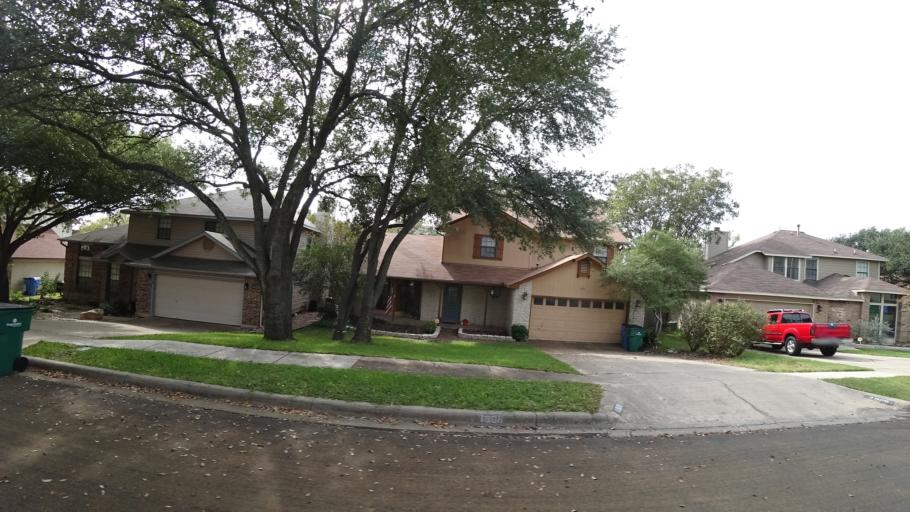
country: US
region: Texas
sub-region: Travis County
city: Wells Branch
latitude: 30.4377
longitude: -97.6789
